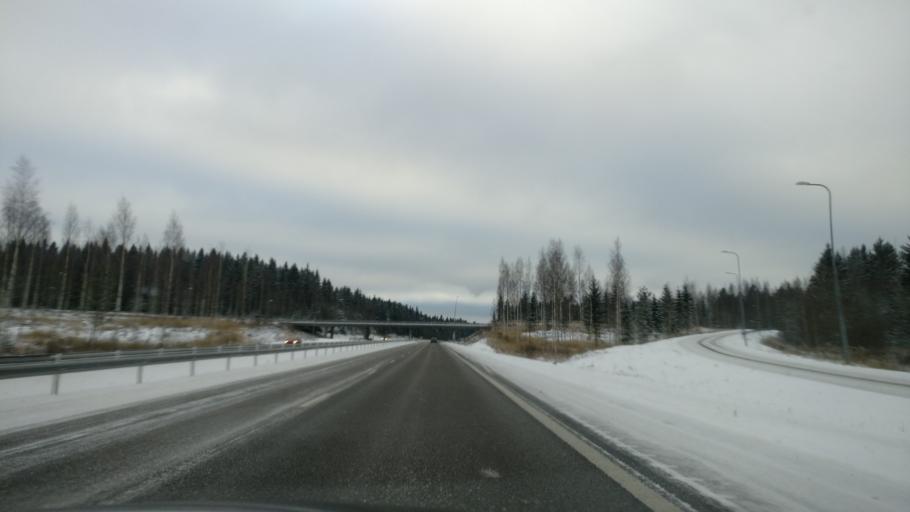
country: FI
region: Paijanne Tavastia
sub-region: Lahti
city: Lahti
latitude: 60.9993
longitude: 25.7879
